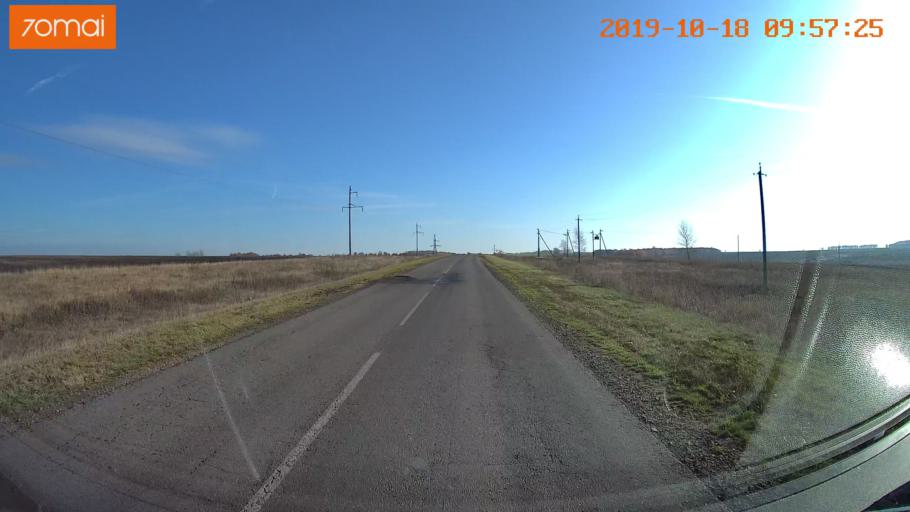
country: RU
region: Tula
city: Kurkino
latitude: 53.3767
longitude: 38.4159
